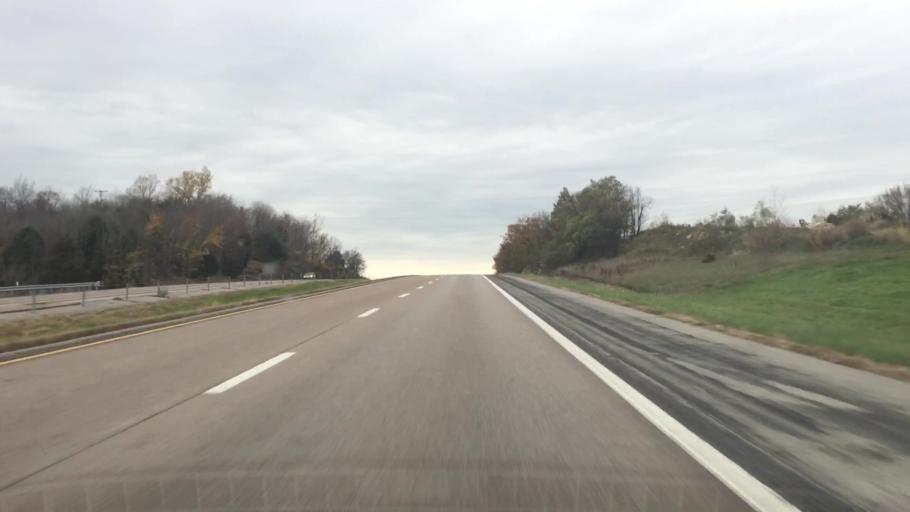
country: US
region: Missouri
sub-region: Boone County
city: Ashland
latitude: 38.6724
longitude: -92.2376
